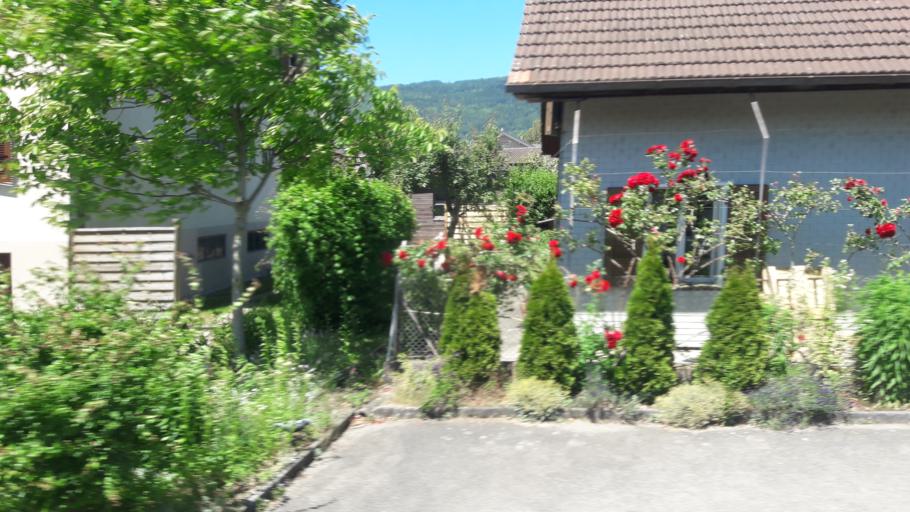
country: CH
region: Bern
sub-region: Biel/Bienne District
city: Bellmund
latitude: 47.1021
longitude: 7.2196
